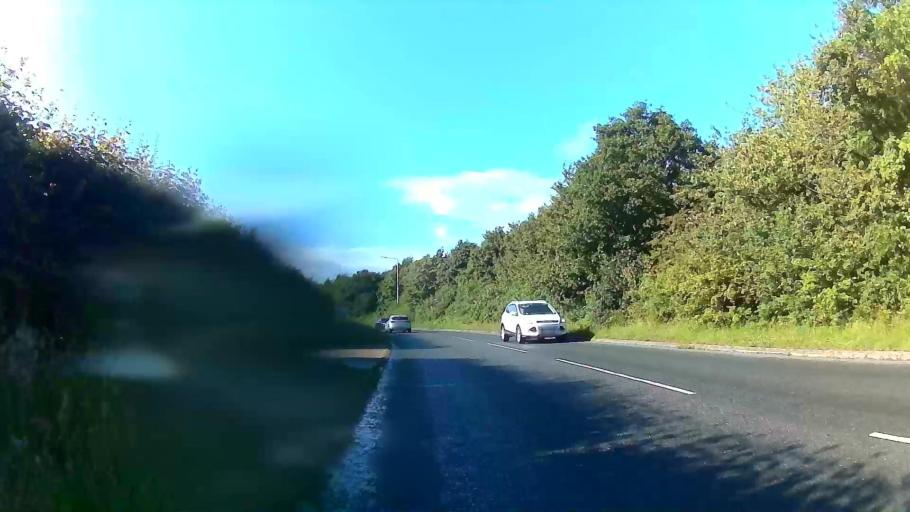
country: GB
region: England
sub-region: Essex
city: Writtle
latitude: 51.7271
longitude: 0.4104
